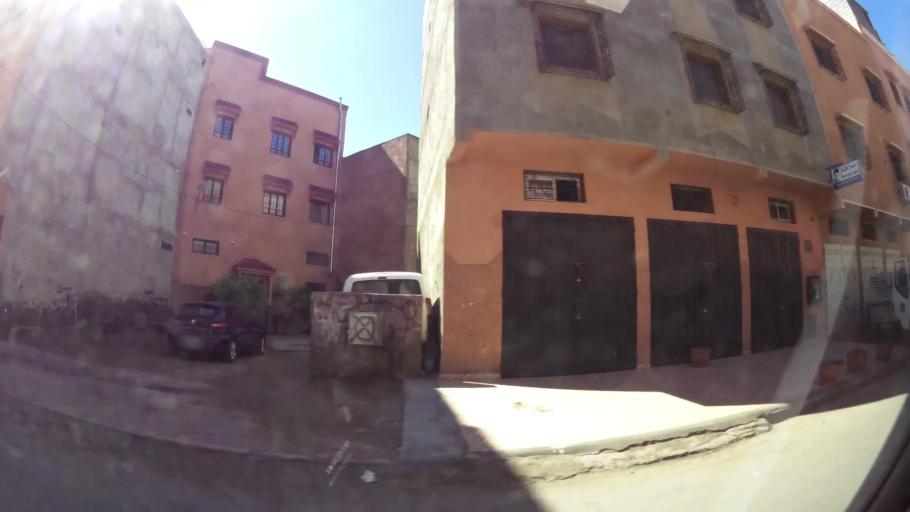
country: MA
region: Marrakech-Tensift-Al Haouz
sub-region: Marrakech
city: Marrakesh
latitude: 31.6462
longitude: -7.9806
